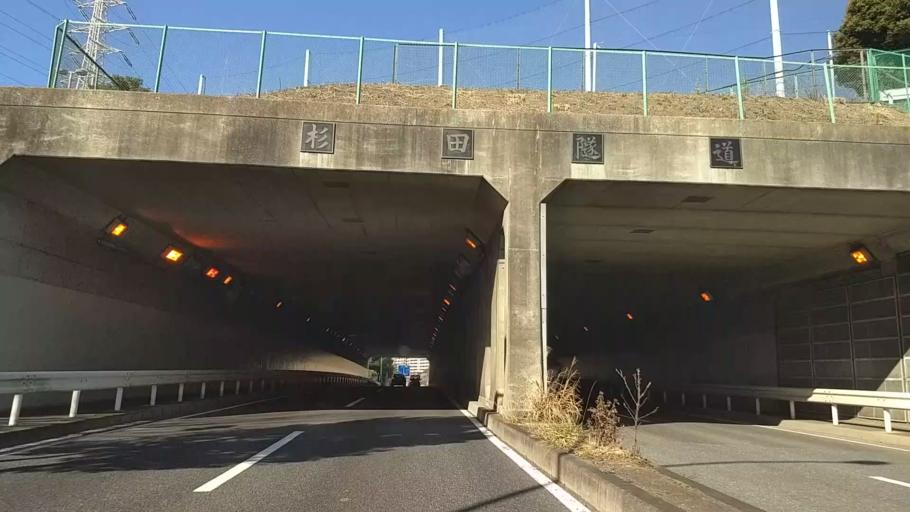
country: JP
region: Kanagawa
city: Yokohama
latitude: 35.3772
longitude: 139.6122
